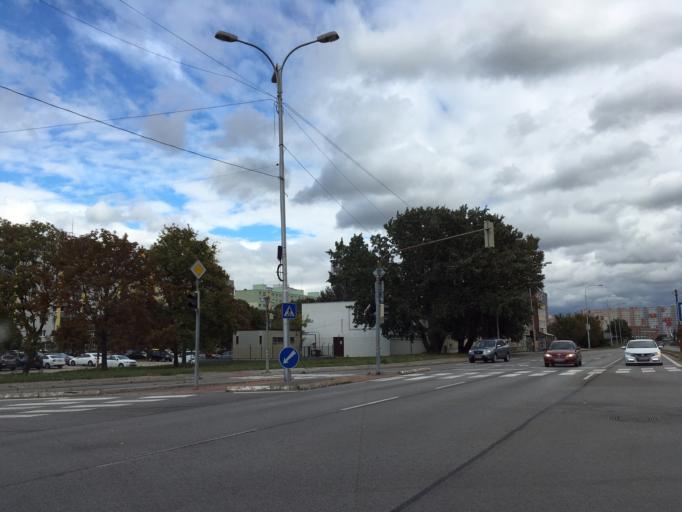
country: SK
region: Bratislavsky
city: Bratislava
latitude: 48.1239
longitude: 17.1062
